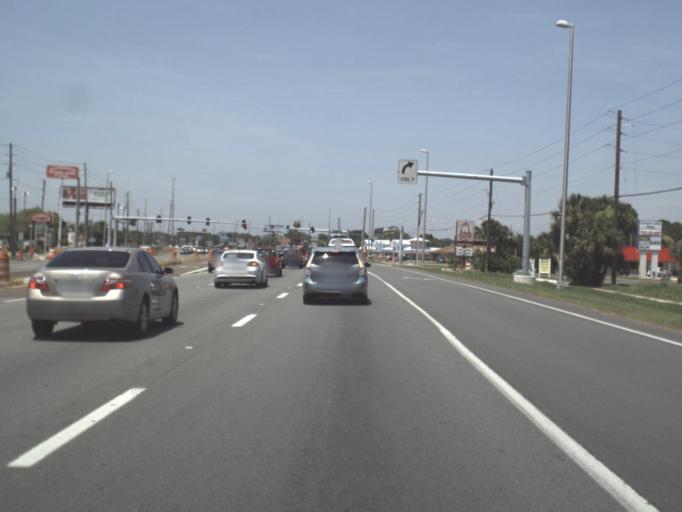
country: US
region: Florida
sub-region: Pasco County
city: Jasmine Estates
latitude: 28.3081
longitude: -82.7005
